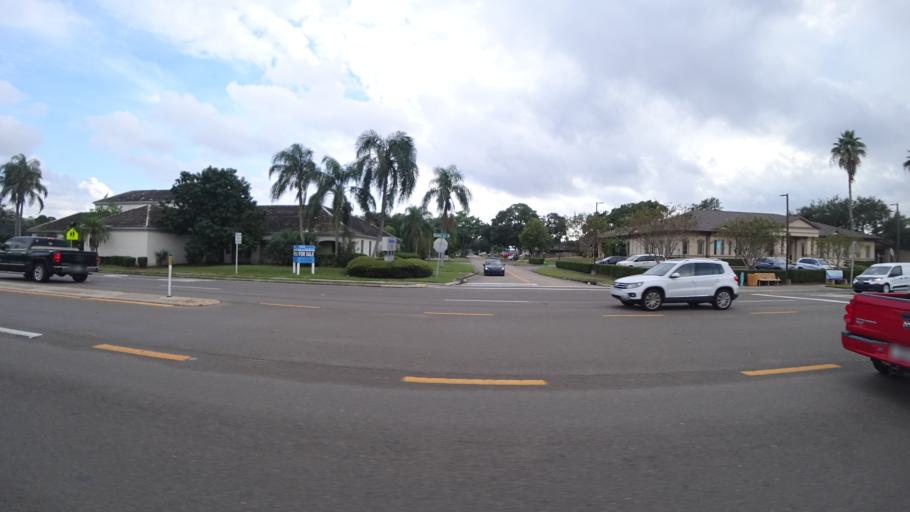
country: US
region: Florida
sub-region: Manatee County
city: West Bradenton
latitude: 27.4960
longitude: -82.6049
